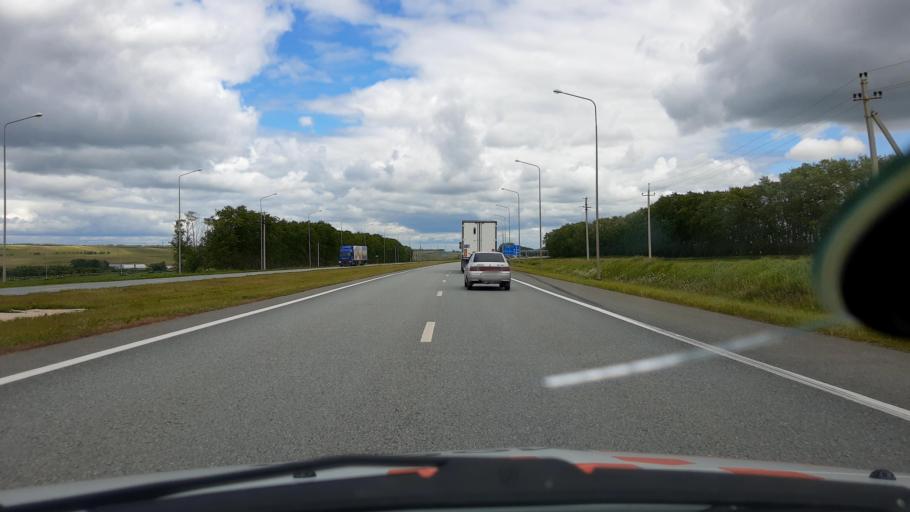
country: RU
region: Bashkortostan
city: Alekseyevka
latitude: 54.7209
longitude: 54.9062
